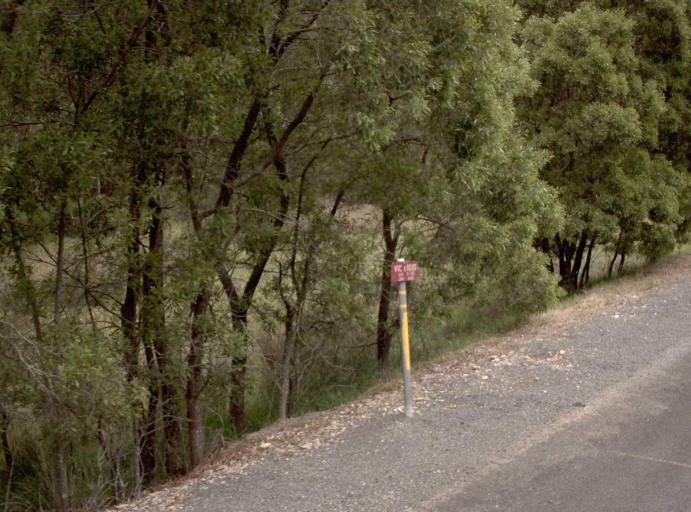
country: AU
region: New South Wales
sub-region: Bombala
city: Bombala
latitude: -37.2313
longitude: 149.2739
